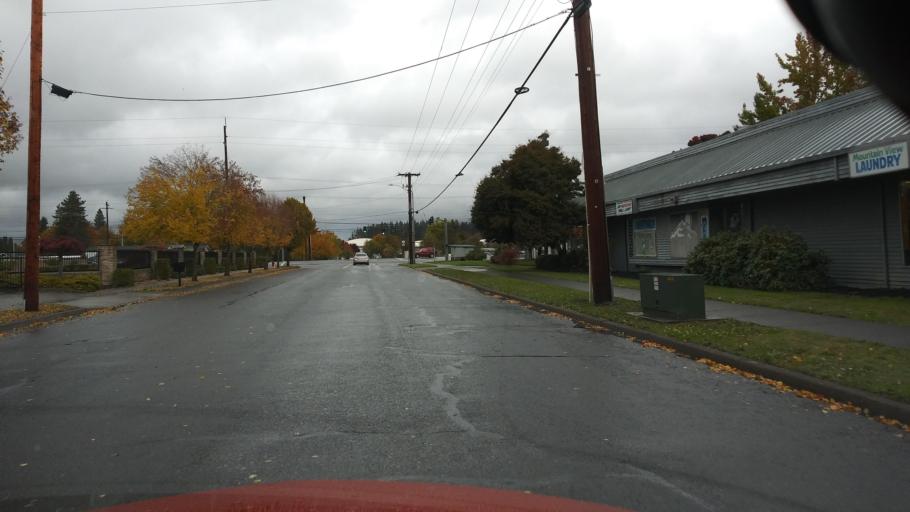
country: US
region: Oregon
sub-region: Washington County
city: Cornelius
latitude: 45.5191
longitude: -123.0758
